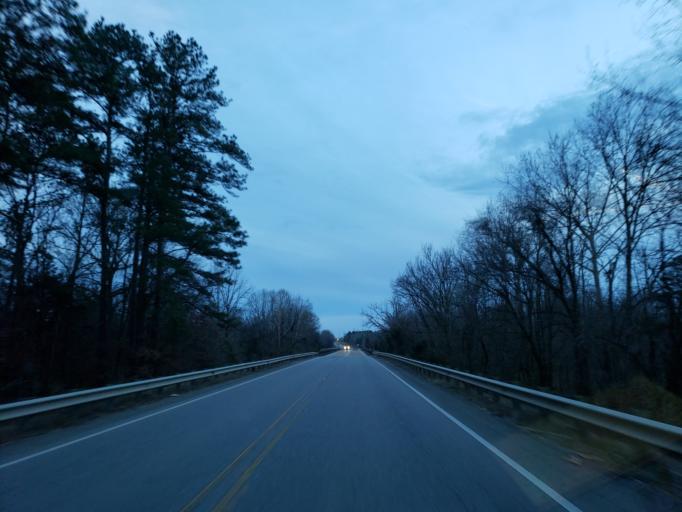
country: US
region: Alabama
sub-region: Sumter County
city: Livingston
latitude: 32.8080
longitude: -88.3119
